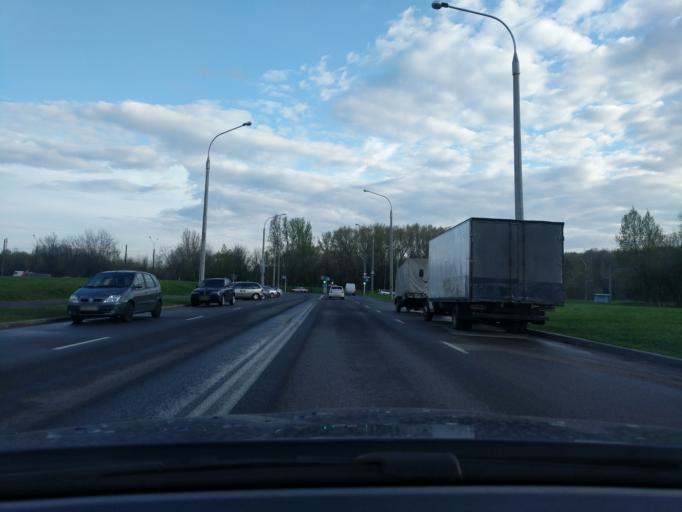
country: BY
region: Minsk
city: Novoye Medvezhino
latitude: 53.8950
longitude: 27.4749
